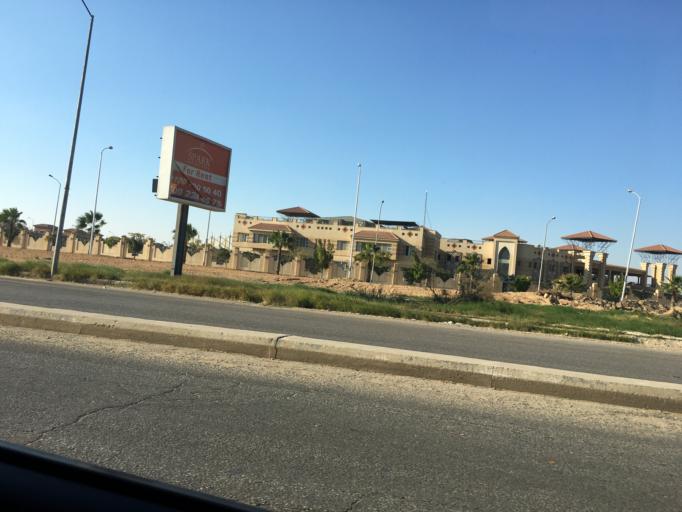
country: EG
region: Al Jizah
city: Madinat Sittah Uktubar
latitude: 29.9960
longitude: 30.9529
